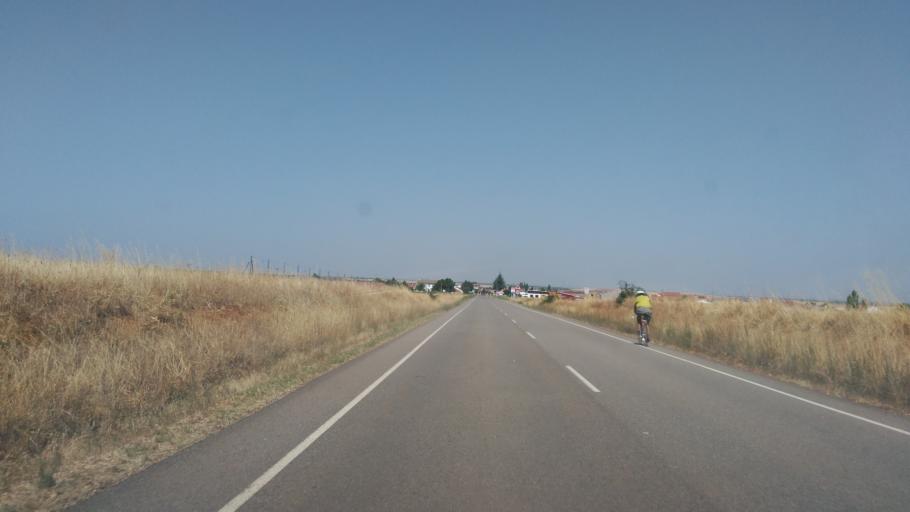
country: ES
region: Castille and Leon
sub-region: Provincia de Salamanca
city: Abusejo
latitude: 40.7041
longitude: -6.1388
